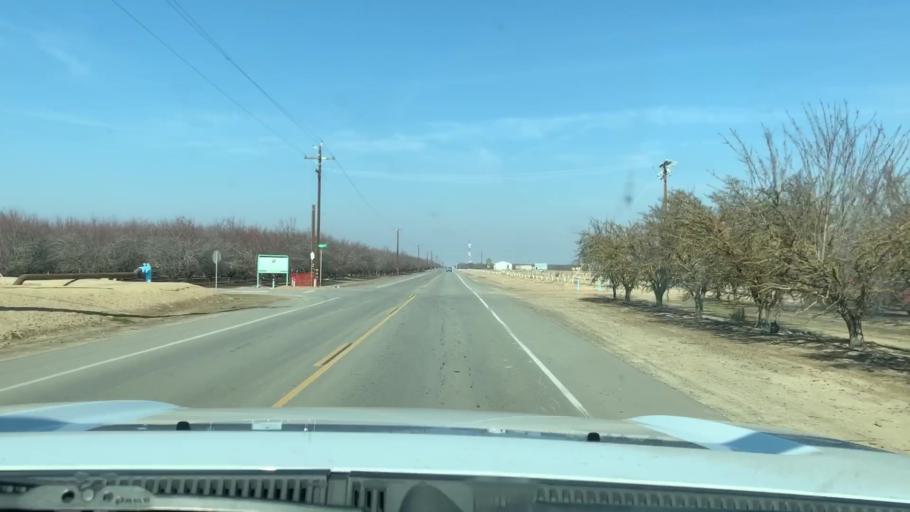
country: US
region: California
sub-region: Kern County
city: Wasco
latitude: 35.5718
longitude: -119.4740
